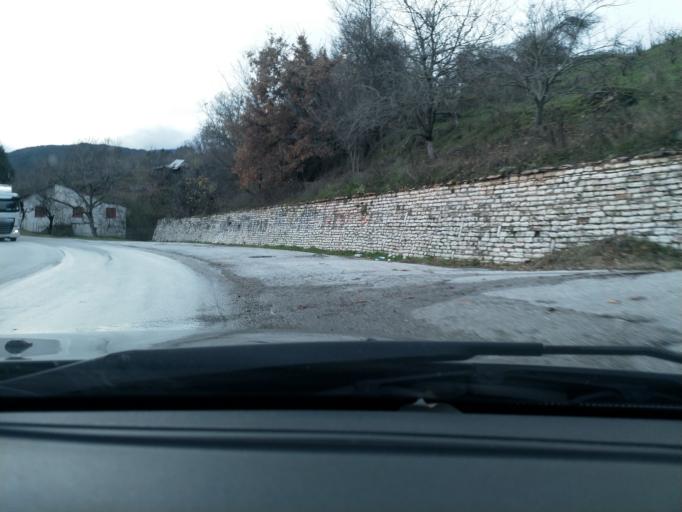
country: GR
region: Epirus
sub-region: Nomos Ioanninon
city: Metsovo
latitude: 39.8099
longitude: 21.3457
